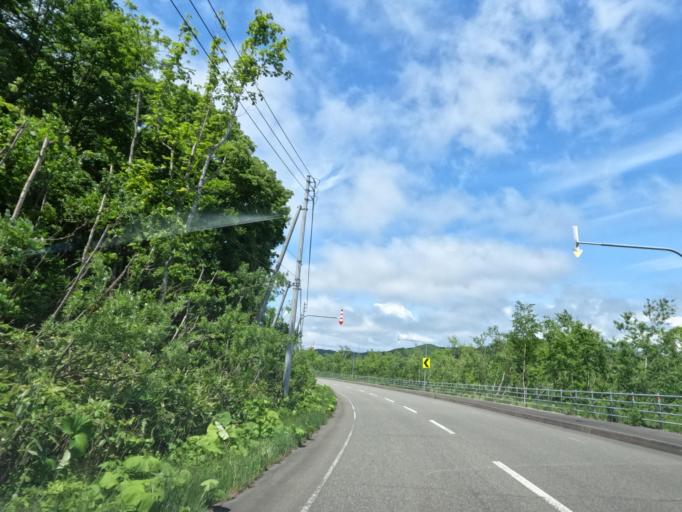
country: JP
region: Hokkaido
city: Tobetsu
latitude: 43.3284
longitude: 141.5727
